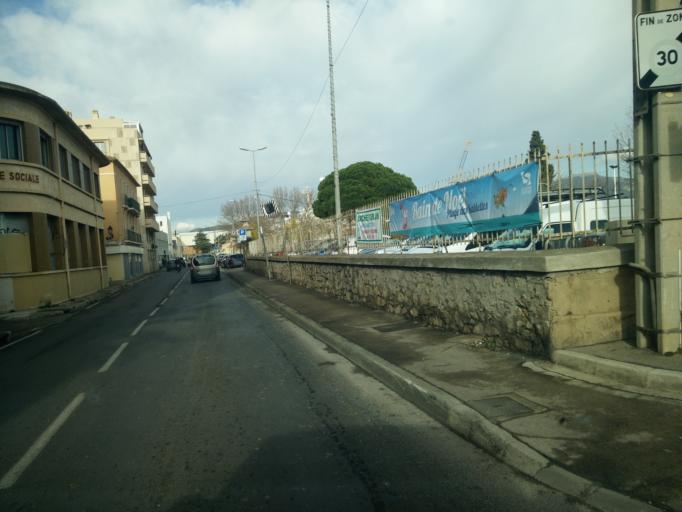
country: FR
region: Provence-Alpes-Cote d'Azur
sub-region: Departement du Var
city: La Seyne-sur-Mer
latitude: 43.1028
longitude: 5.8818
